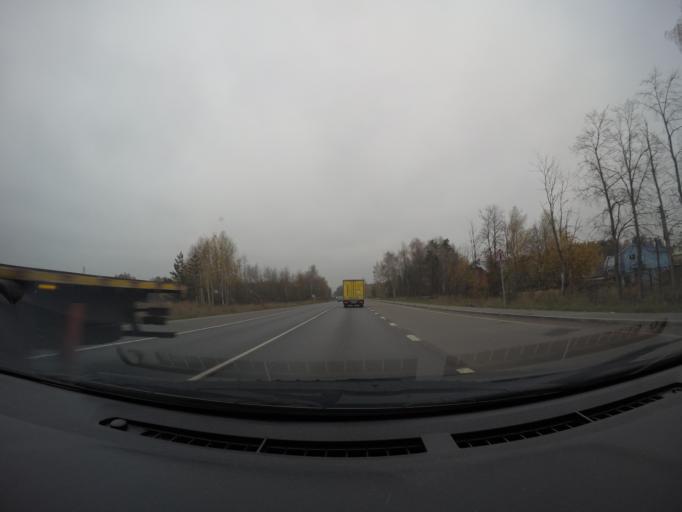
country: RU
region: Moskovskaya
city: Malyshevo
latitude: 55.5341
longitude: 38.4027
